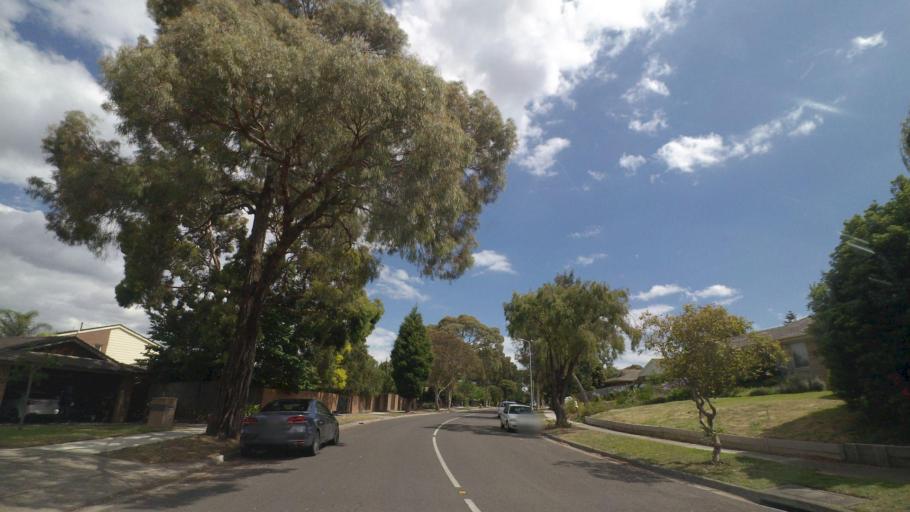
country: AU
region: Victoria
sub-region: Knox
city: Wantirna
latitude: -37.8627
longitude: 145.2226
